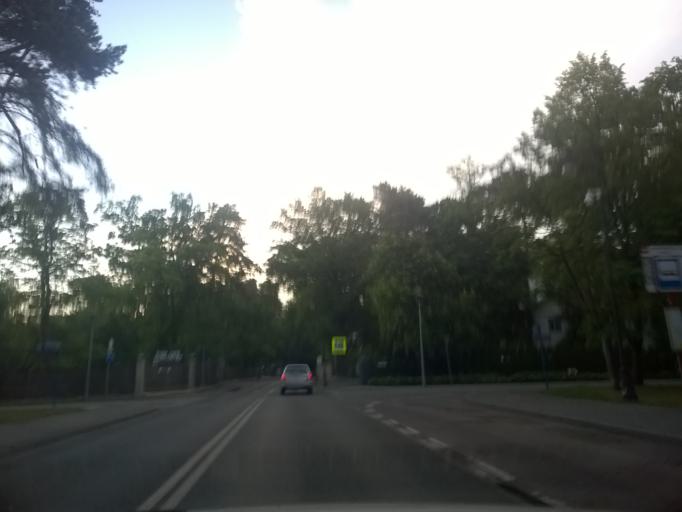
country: PL
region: Masovian Voivodeship
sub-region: Powiat piaseczynski
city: Konstancin-Jeziorna
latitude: 52.0838
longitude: 21.1194
